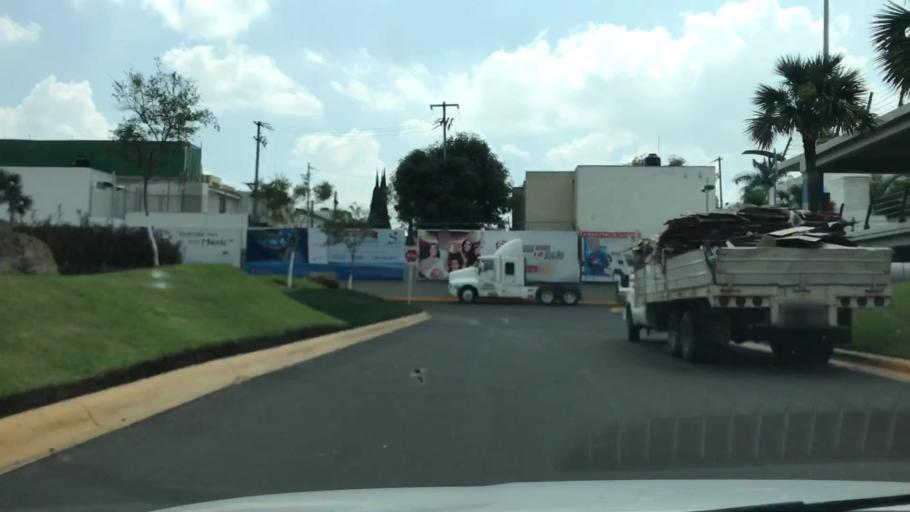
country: MX
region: Jalisco
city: Guadalajara
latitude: 20.6761
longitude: -103.4287
